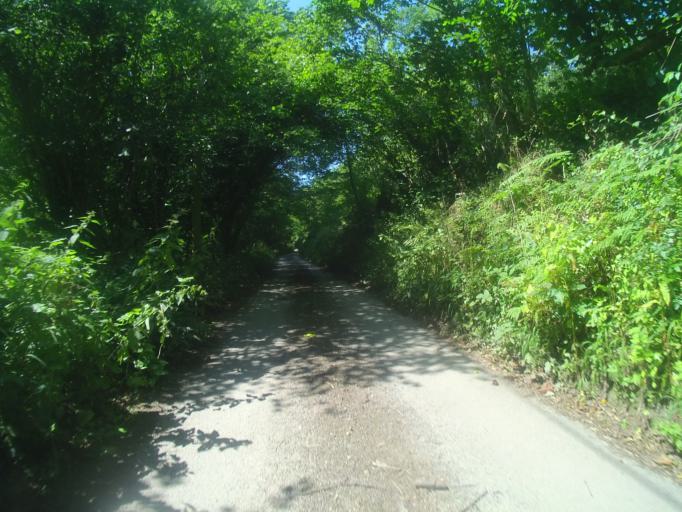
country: GB
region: England
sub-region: Devon
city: Dartmouth
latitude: 50.3576
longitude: -3.6071
